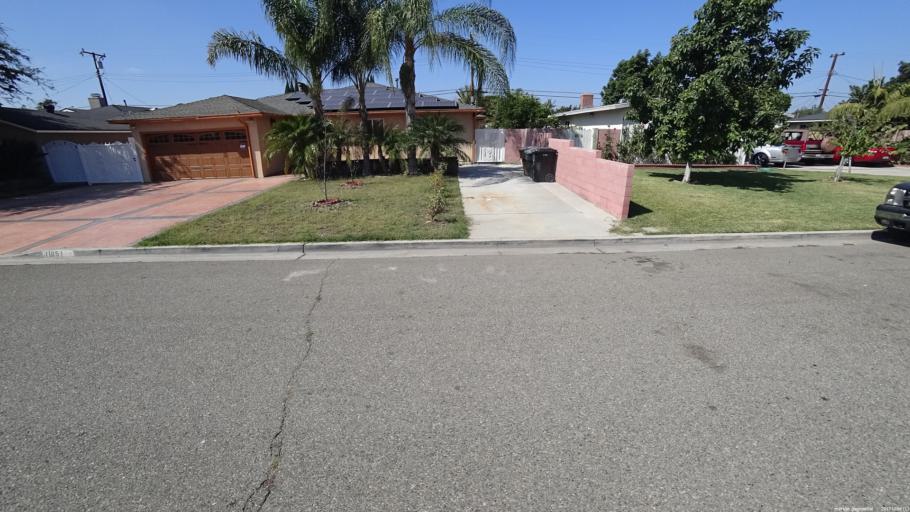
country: US
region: California
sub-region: Orange County
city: Garden Grove
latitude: 33.7935
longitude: -117.9504
